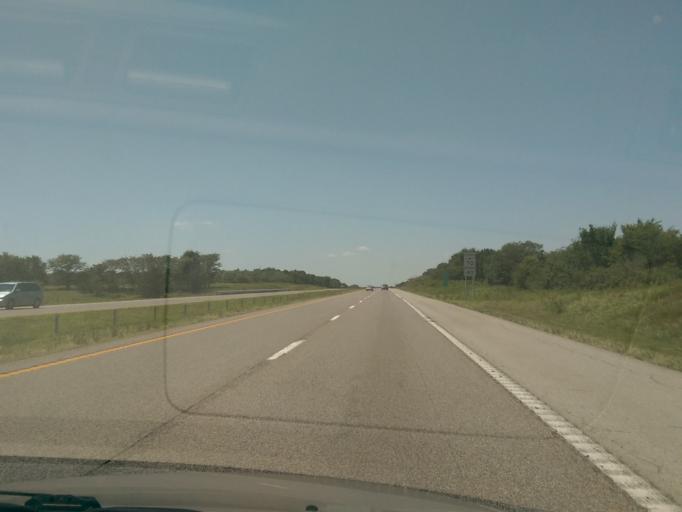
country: US
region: Missouri
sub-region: Saline County
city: Marshall
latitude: 38.9508
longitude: -93.0530
